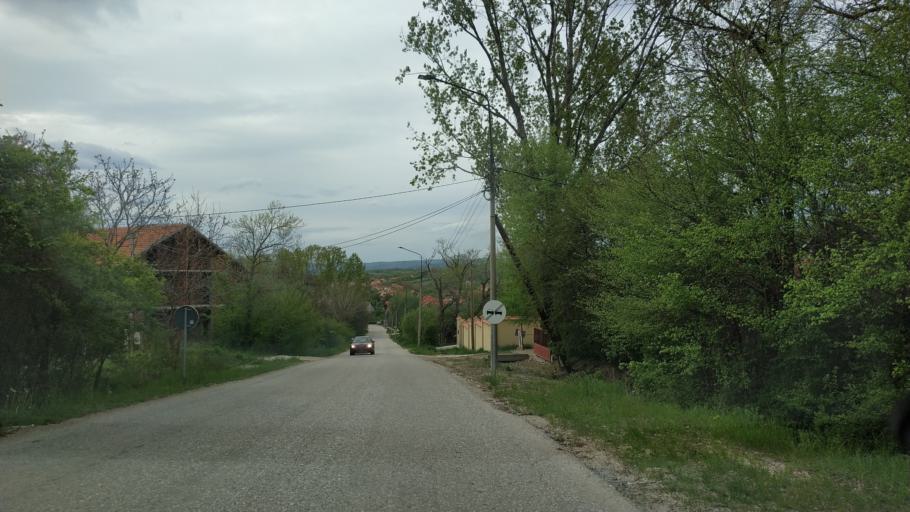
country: RS
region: Central Serbia
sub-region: Zajecarski Okrug
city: Soko Banja
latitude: 43.6433
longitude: 21.8885
